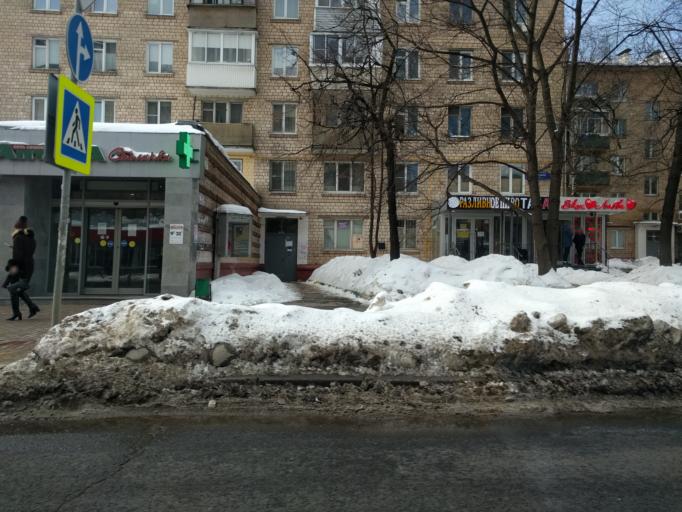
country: RU
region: Moskovskaya
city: Izmaylovo
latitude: 55.7951
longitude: 37.7993
